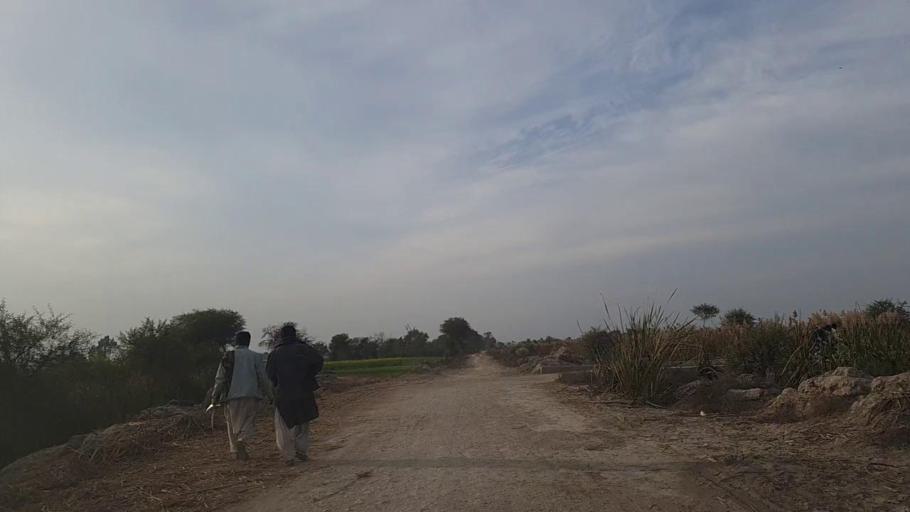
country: PK
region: Sindh
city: Daur
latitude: 26.5267
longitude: 68.4059
